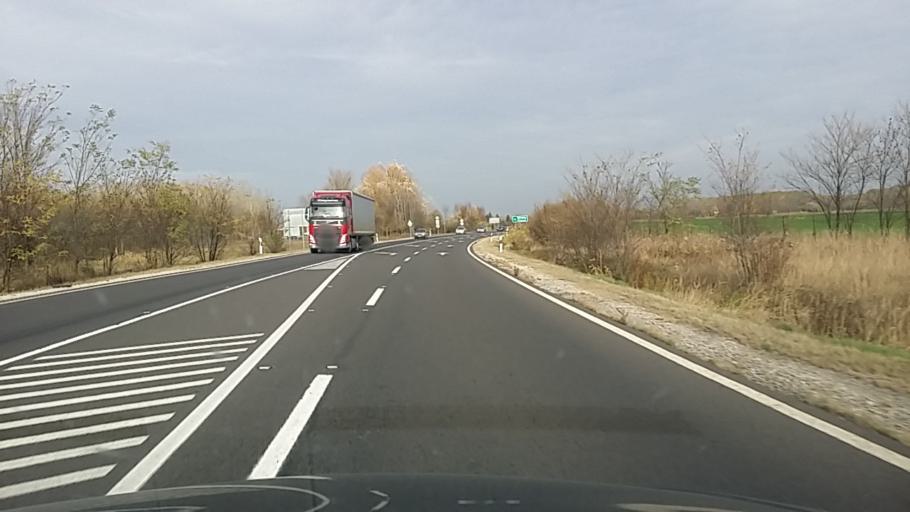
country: HU
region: Szabolcs-Szatmar-Bereg
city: Nyirbogdany
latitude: 48.0409
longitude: 21.8629
